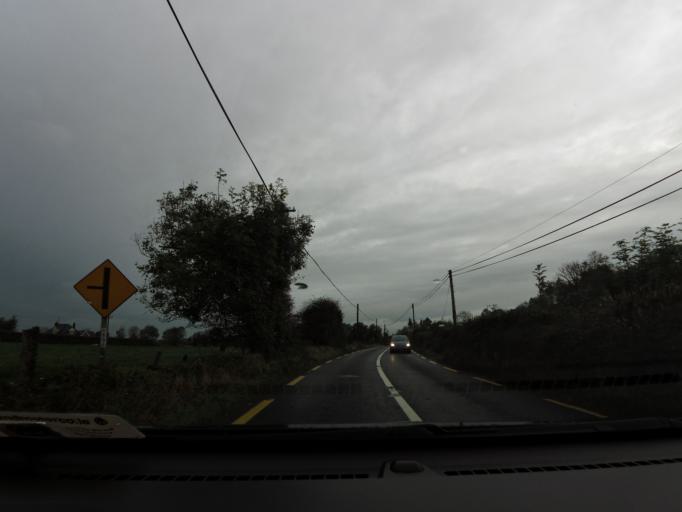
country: IE
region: Connaught
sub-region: County Galway
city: Tuam
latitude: 53.5431
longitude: -8.8100
